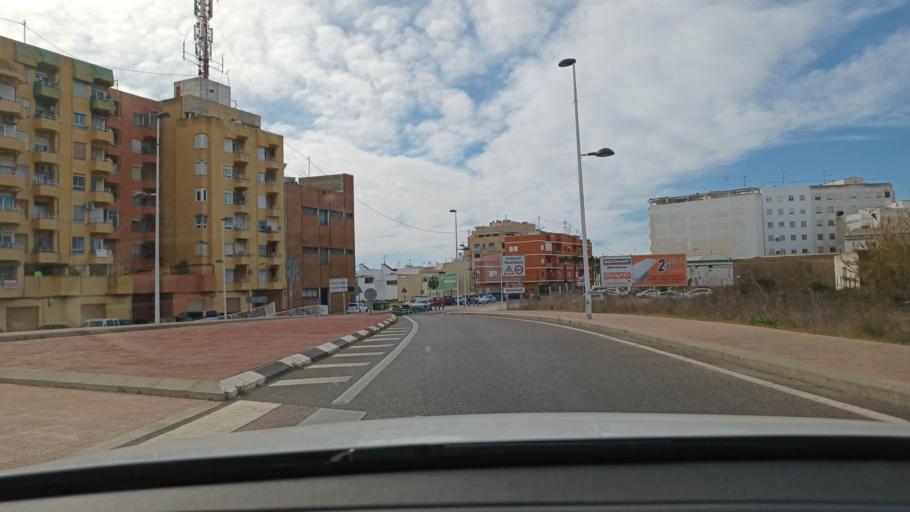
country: ES
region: Valencia
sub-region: Provincia de Valencia
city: Almussafes
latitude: 39.2900
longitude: -0.4200
